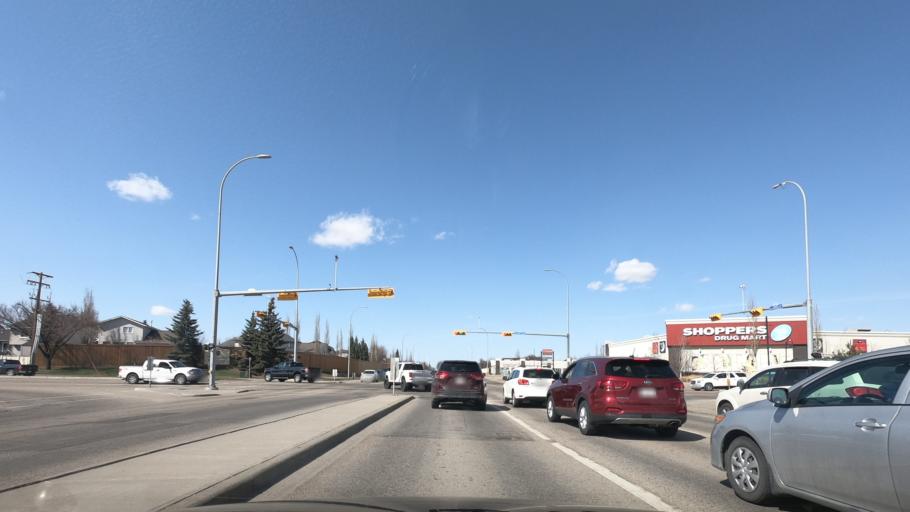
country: CA
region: Alberta
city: Airdrie
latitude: 51.2923
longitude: -114.0251
